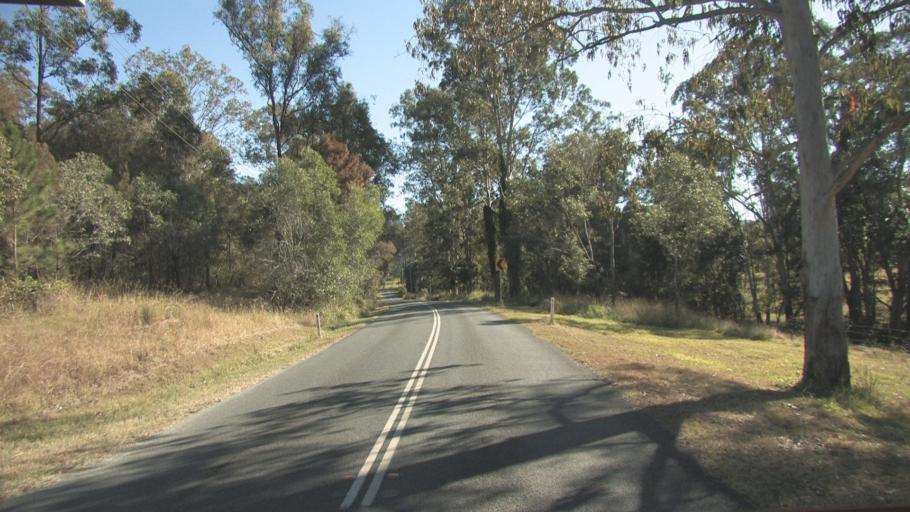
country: AU
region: Queensland
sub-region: Logan
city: Windaroo
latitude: -27.8067
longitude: 153.1703
